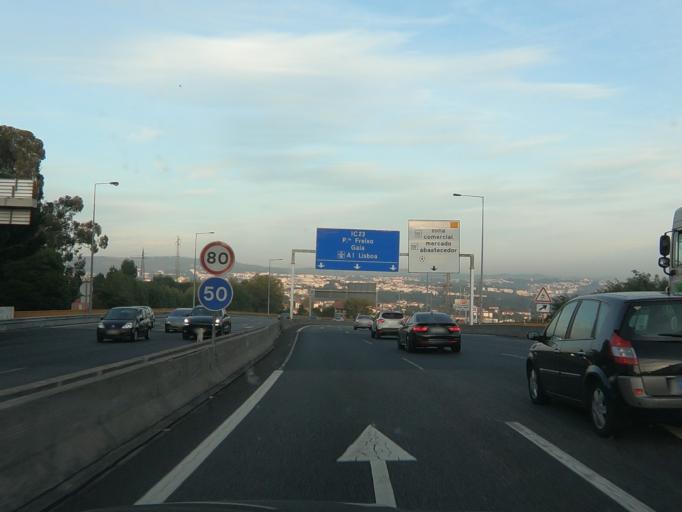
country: PT
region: Porto
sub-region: Maia
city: Pedroucos
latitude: 41.1659
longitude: -8.5873
